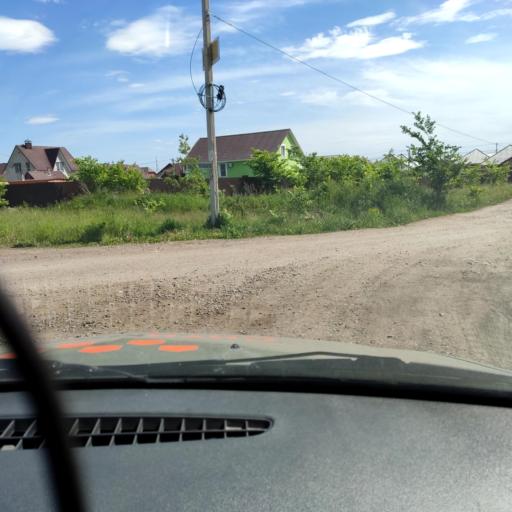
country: RU
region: Bashkortostan
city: Ufa
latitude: 54.6810
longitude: 56.0882
